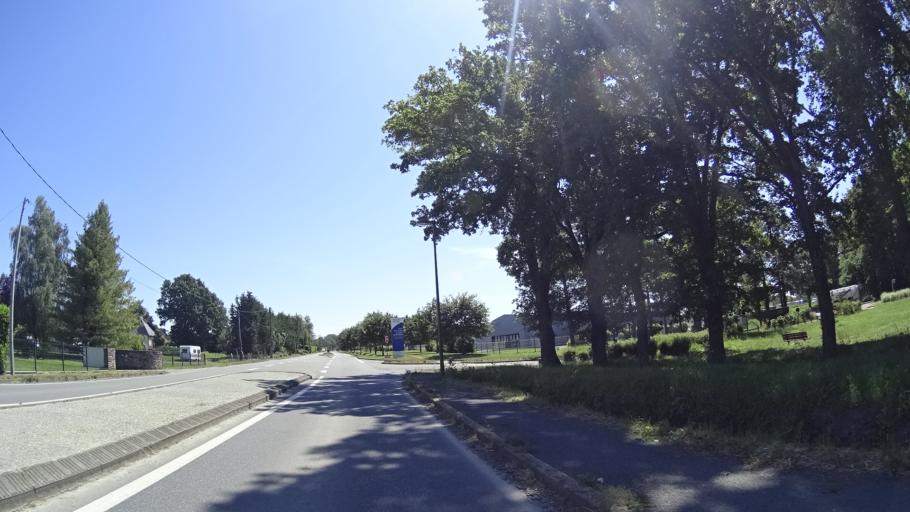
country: FR
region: Brittany
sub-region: Departement d'Ille-et-Vilaine
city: Messac
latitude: 47.8254
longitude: -1.7906
